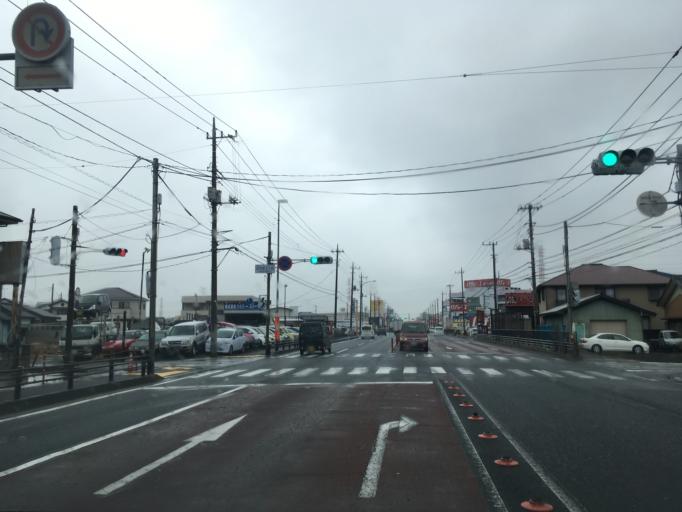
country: JP
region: Saitama
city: Koshigaya
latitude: 35.8857
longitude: 139.7732
